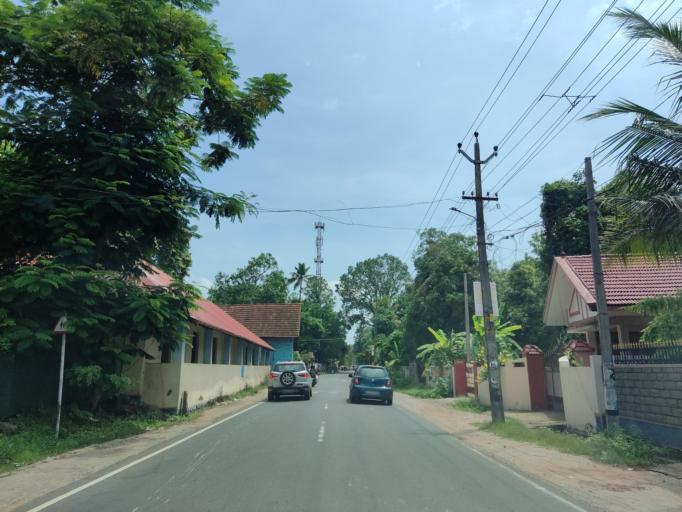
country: IN
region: Kerala
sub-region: Alappuzha
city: Chengannur
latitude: 9.3102
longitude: 76.6010
